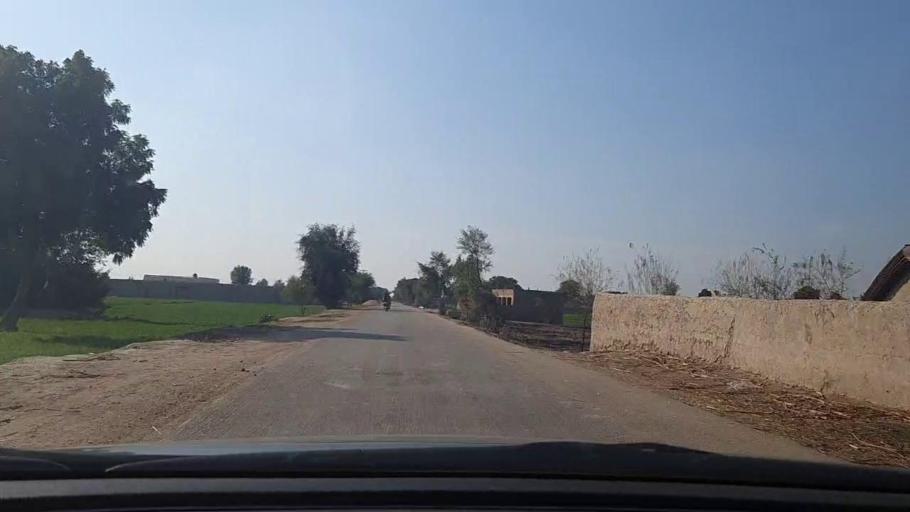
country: PK
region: Sindh
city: Daulatpur
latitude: 26.3195
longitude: 68.0471
